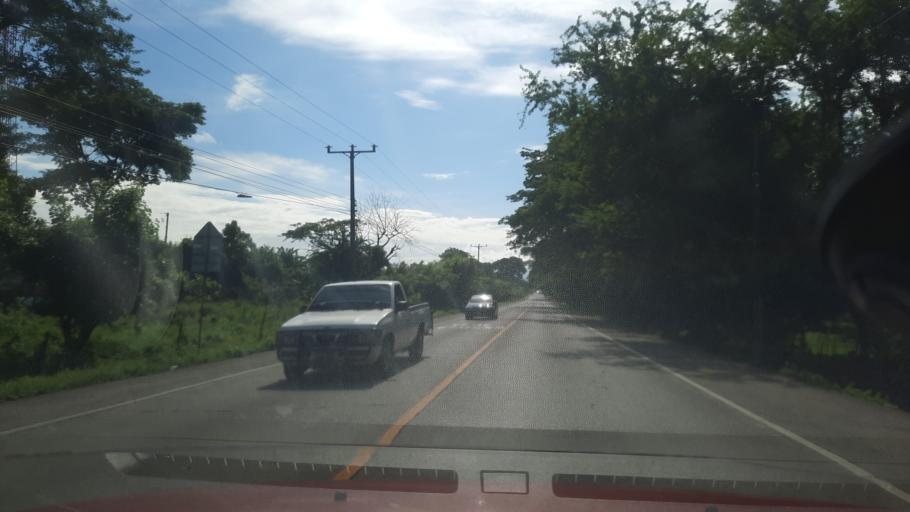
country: SV
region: La Paz
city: Zacatecoluca
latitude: 13.4367
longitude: -88.7824
